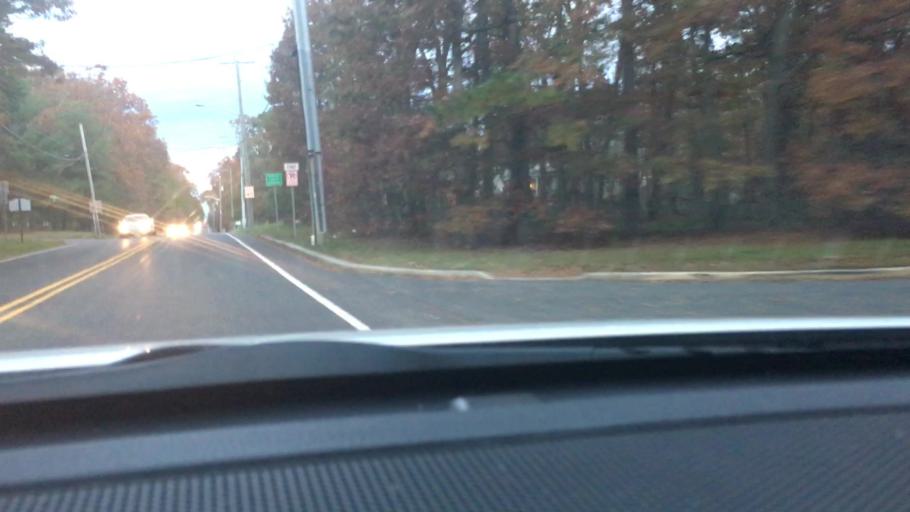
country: US
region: New Jersey
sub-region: Atlantic County
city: Absecon
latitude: 39.4436
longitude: -74.4974
